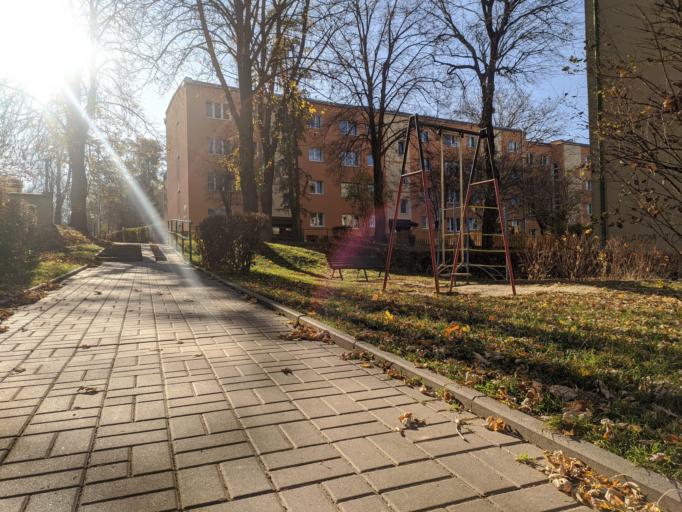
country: PL
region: Lublin Voivodeship
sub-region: Powiat lubelski
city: Lublin
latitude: 51.2543
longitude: 22.5319
